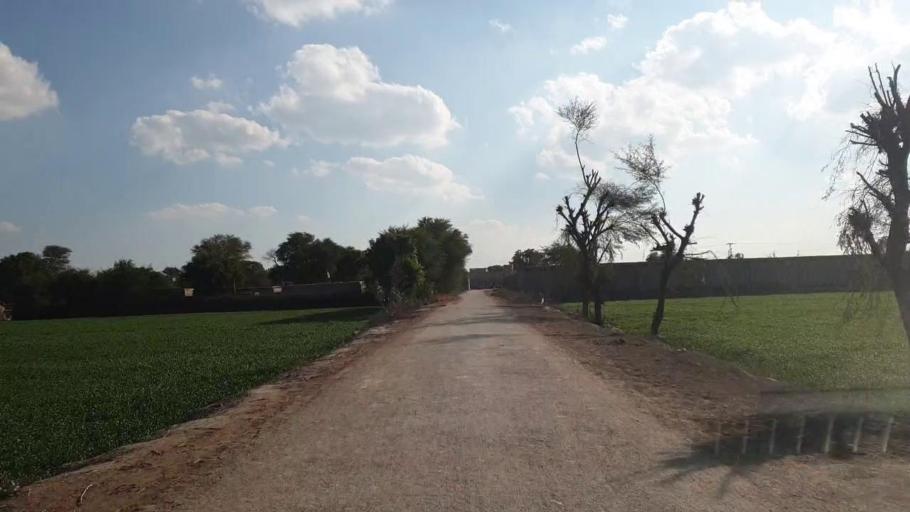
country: PK
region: Sindh
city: Shahpur Chakar
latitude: 26.1016
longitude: 68.5926
